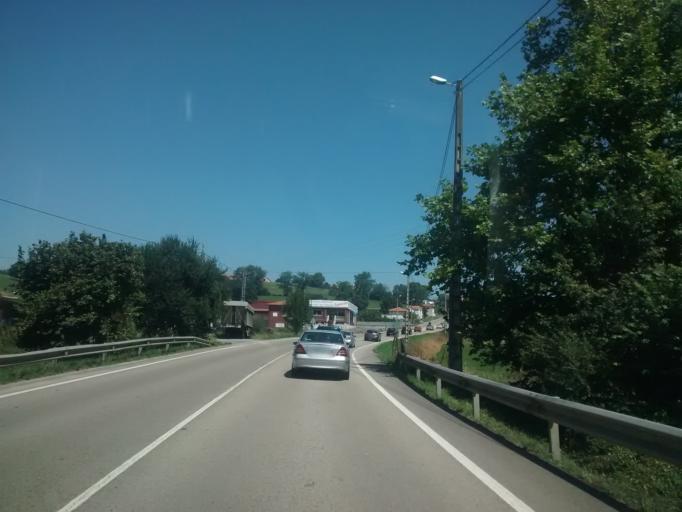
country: ES
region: Cantabria
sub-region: Provincia de Cantabria
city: San Miguel de Meruelo
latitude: 43.4385
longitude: -3.5692
